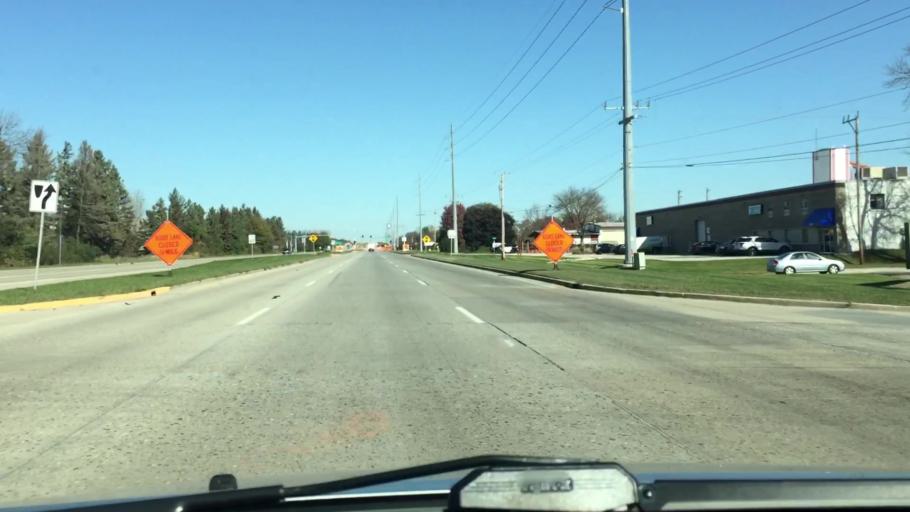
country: US
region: Wisconsin
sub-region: Waukesha County
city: Waukesha
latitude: 43.0621
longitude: -88.2056
